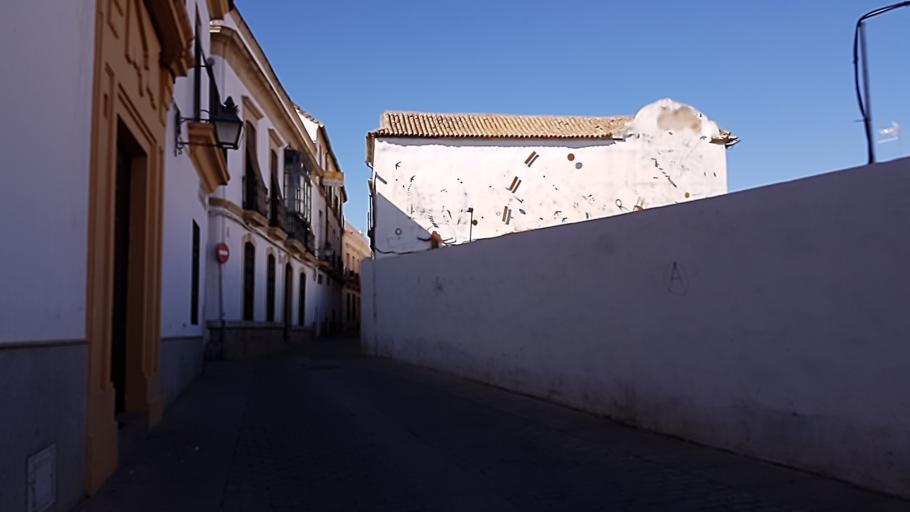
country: ES
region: Andalusia
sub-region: Province of Cordoba
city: Cordoba
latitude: 37.8828
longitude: -4.7772
